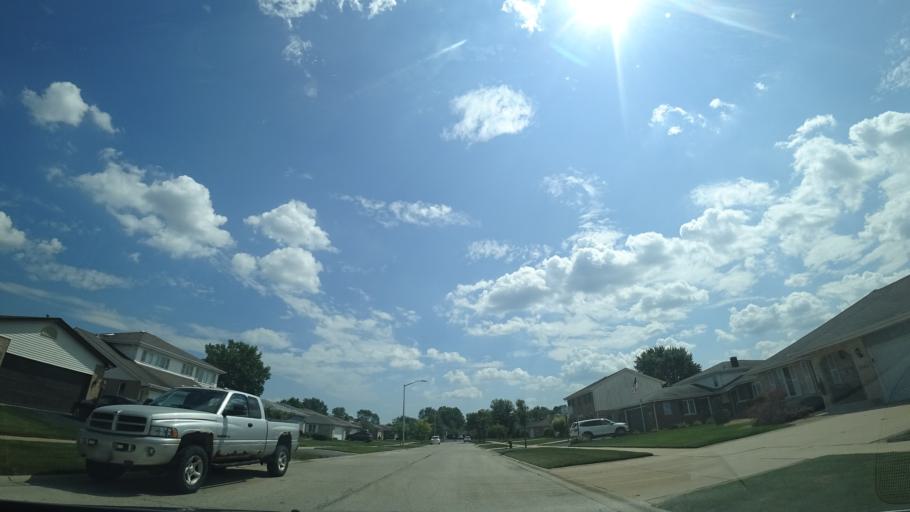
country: US
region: Illinois
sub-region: Cook County
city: Alsip
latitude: 41.6729
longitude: -87.7226
